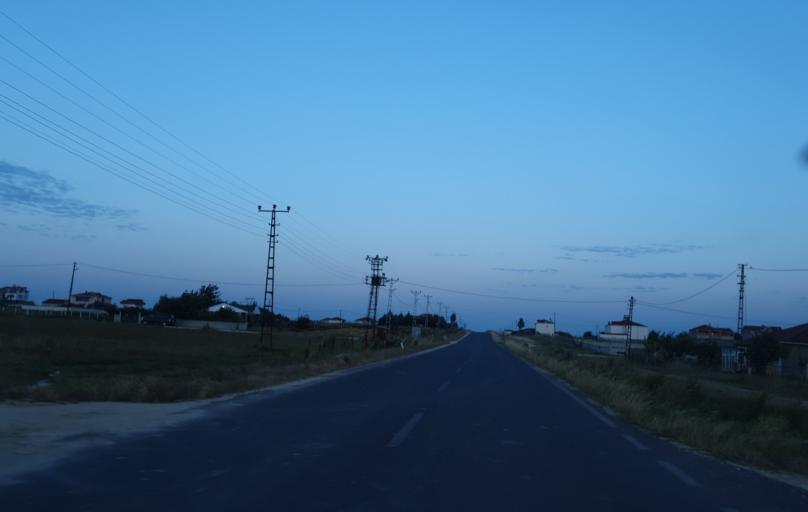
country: TR
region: Tekirdag
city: Velimese
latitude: 41.3437
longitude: 27.8970
